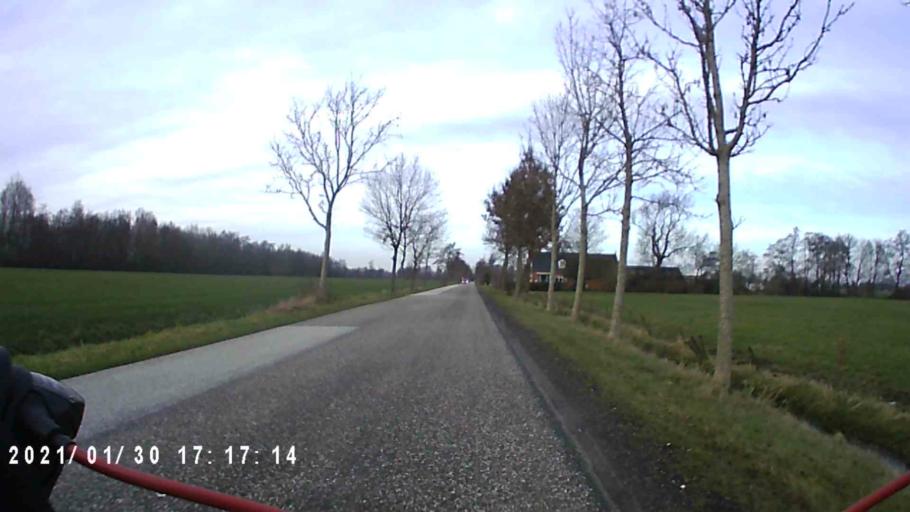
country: NL
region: Groningen
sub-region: Gemeente Leek
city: Leek
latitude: 53.1814
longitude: 6.3590
